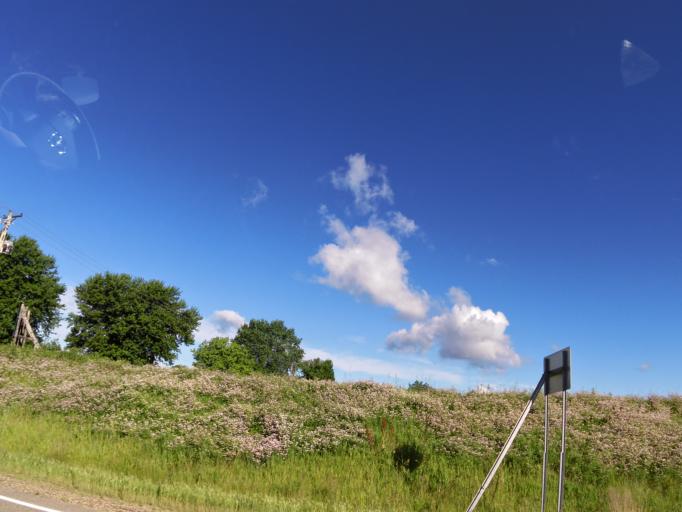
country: US
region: Minnesota
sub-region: Dakota County
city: Hastings
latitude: 44.7787
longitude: -92.8631
